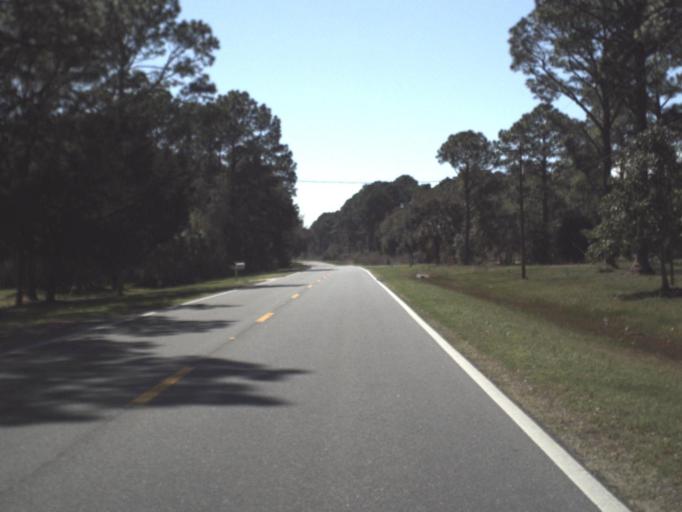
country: US
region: Florida
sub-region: Franklin County
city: Carrabelle
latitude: 29.8883
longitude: -84.5795
